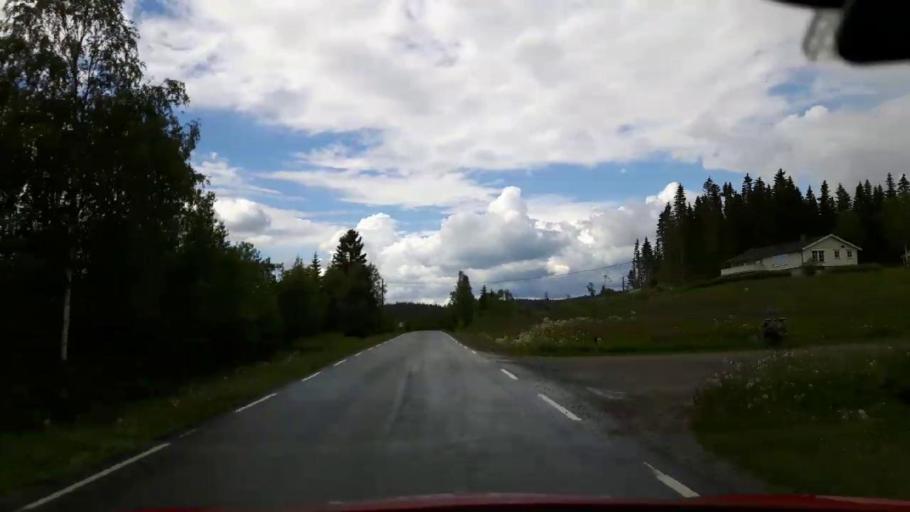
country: NO
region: Nord-Trondelag
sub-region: Lierne
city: Sandvika
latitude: 64.0959
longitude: 14.0383
